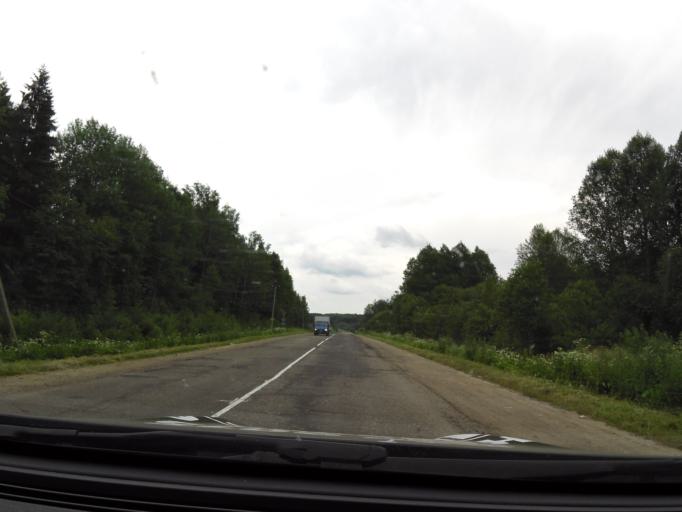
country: RU
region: Kostroma
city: Galich
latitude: 58.4467
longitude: 42.5276
